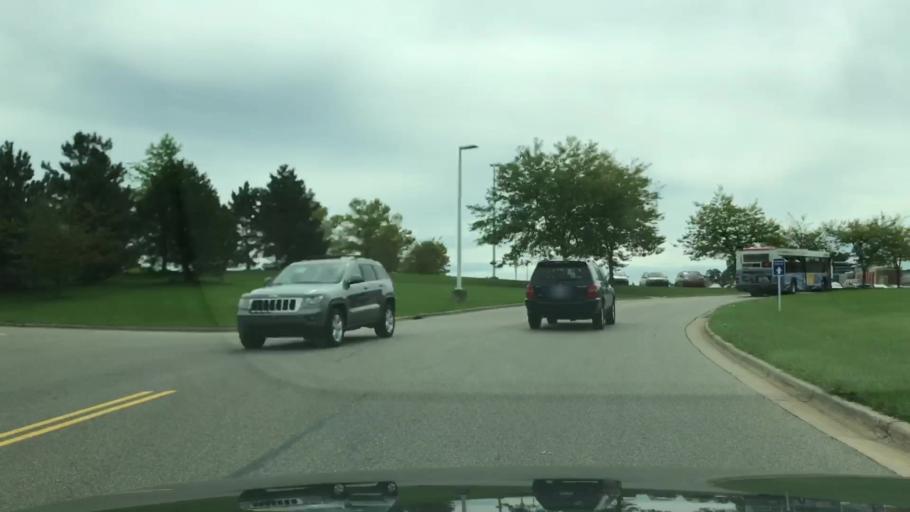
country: US
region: Michigan
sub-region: Kent County
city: Northview
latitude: 42.9985
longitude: -85.5928
